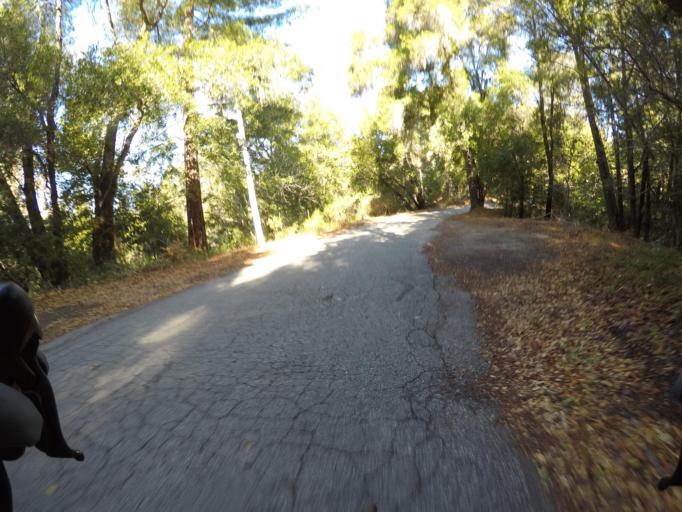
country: US
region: California
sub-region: Santa Cruz County
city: Scotts Valley
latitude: 37.1054
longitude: -121.9921
